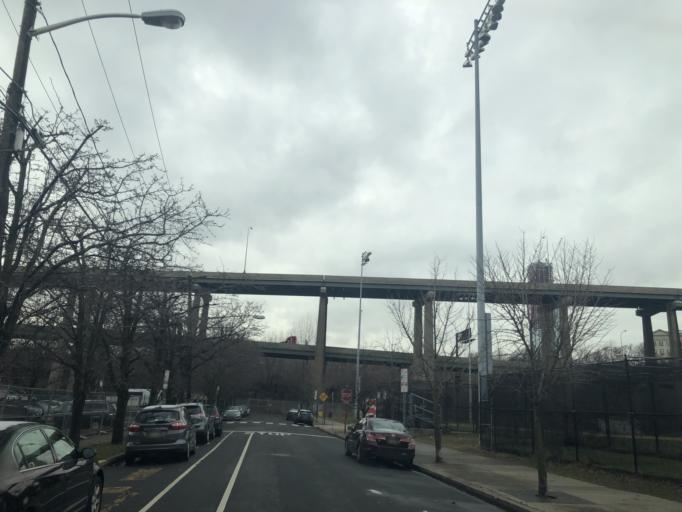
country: US
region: New Jersey
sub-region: Hudson County
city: Hoboken
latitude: 40.7275
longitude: -74.0512
